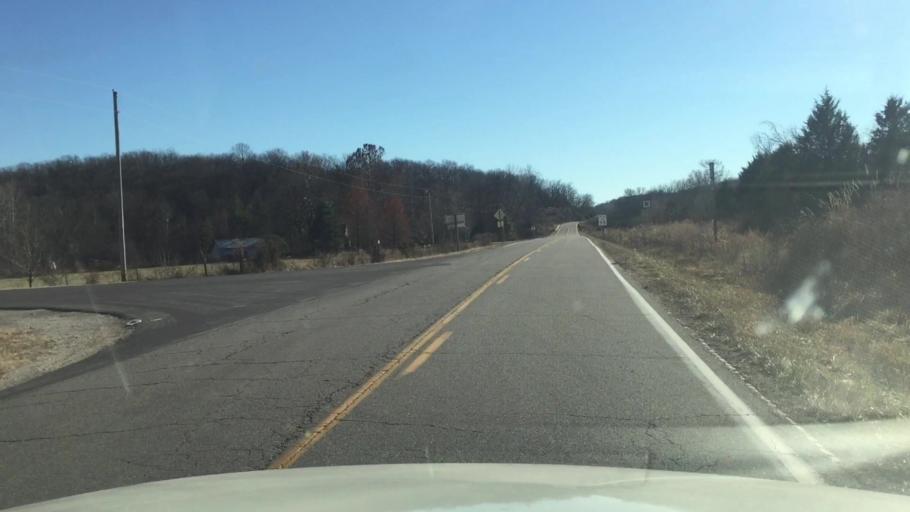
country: US
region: Missouri
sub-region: Miller County
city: Eldon
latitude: 38.3383
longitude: -92.7208
